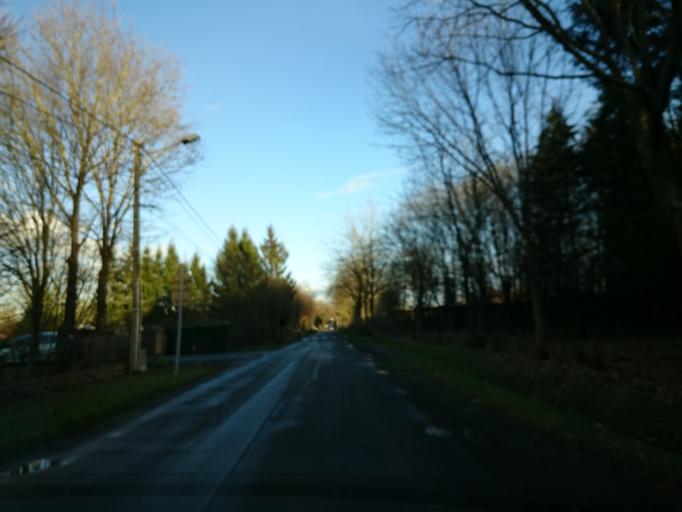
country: FR
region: Brittany
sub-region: Departement d'Ille-et-Vilaine
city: Crevin
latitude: 47.9437
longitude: -1.6602
